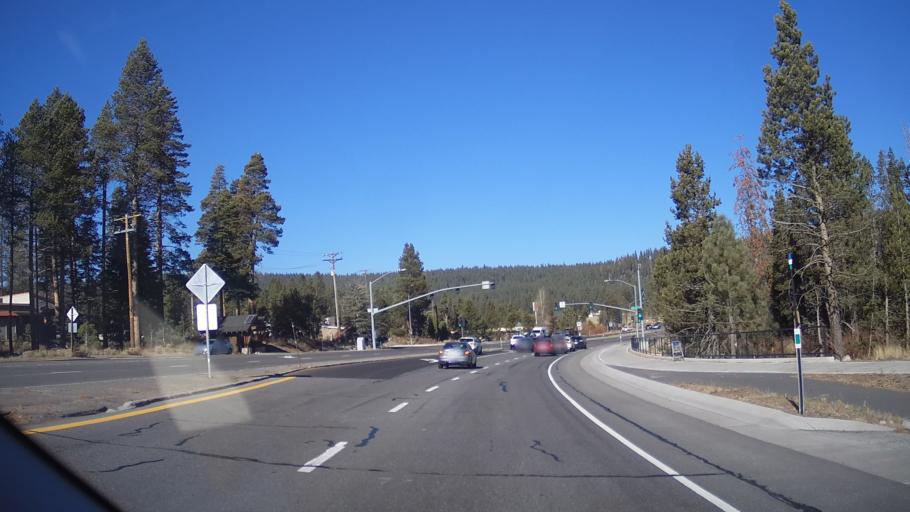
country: US
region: California
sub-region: Nevada County
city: Truckee
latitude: 39.3193
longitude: -120.2071
